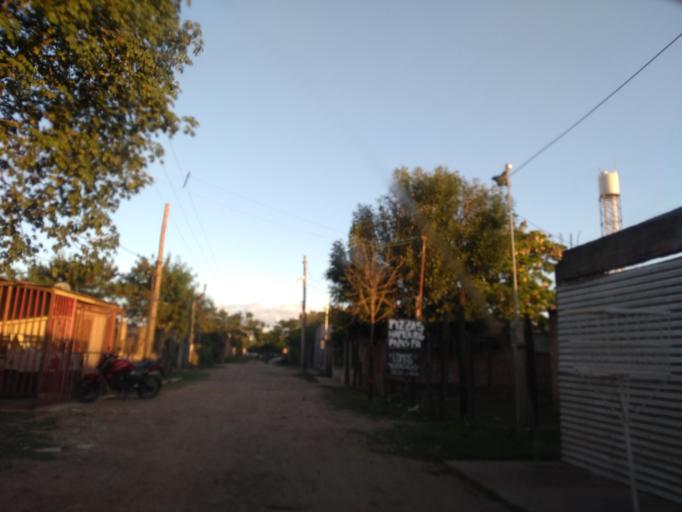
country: AR
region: Chaco
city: Fontana
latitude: -27.4133
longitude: -59.0457
